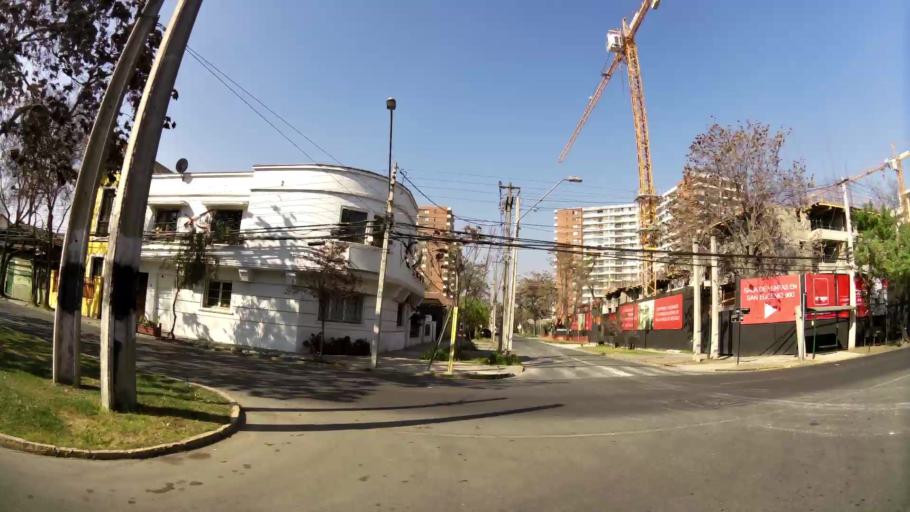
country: CL
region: Santiago Metropolitan
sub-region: Provincia de Santiago
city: Santiago
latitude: -33.4591
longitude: -70.6264
